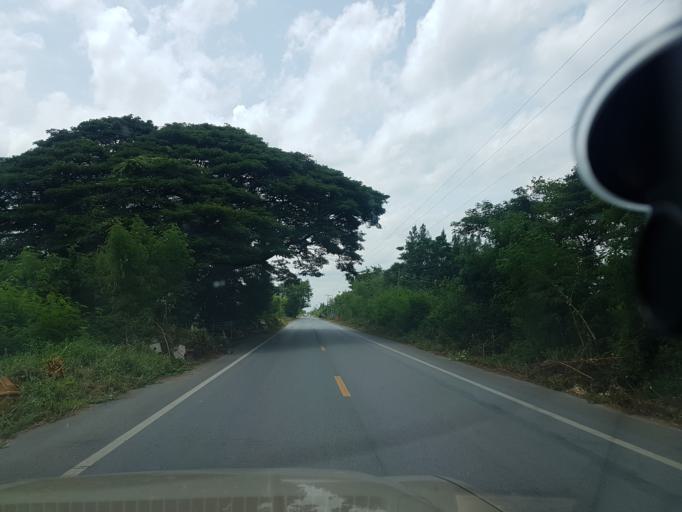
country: TH
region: Sara Buri
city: Nong Khae
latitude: 14.2588
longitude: 100.8918
